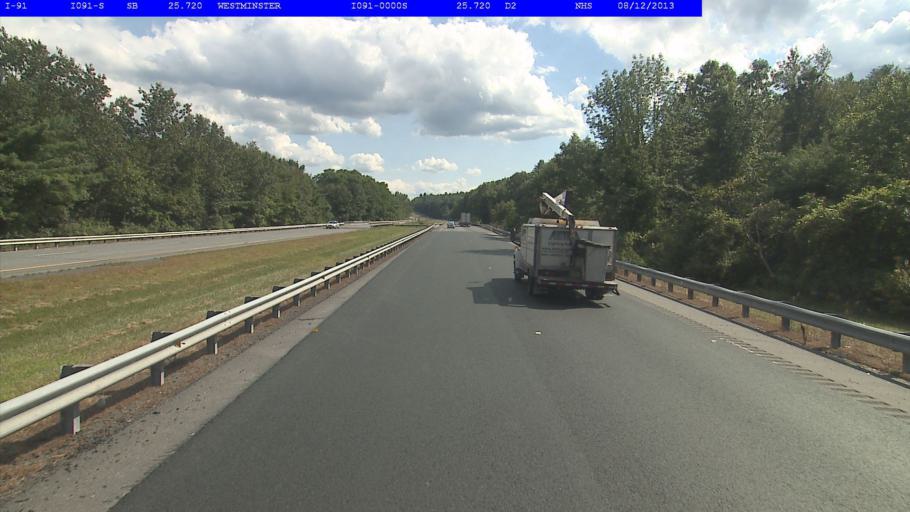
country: US
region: Vermont
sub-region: Windham County
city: Bellows Falls
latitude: 43.0515
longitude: -72.4704
